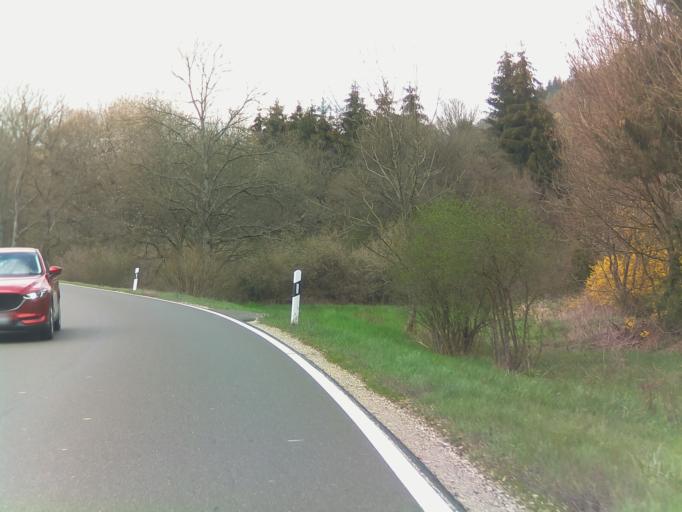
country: DE
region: Rheinland-Pfalz
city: Heinzenberg
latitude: 49.8289
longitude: 7.4882
